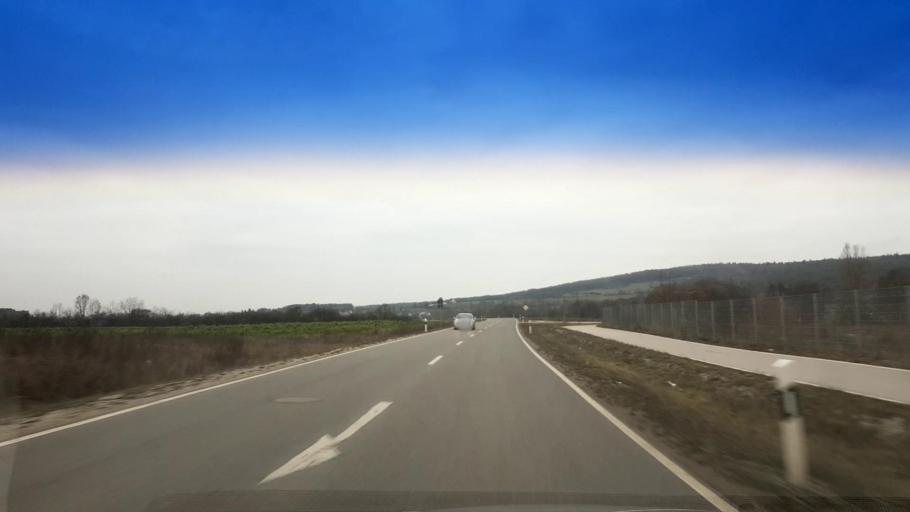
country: DE
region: Bavaria
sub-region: Upper Franconia
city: Pettstadt
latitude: 49.8031
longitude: 10.9457
